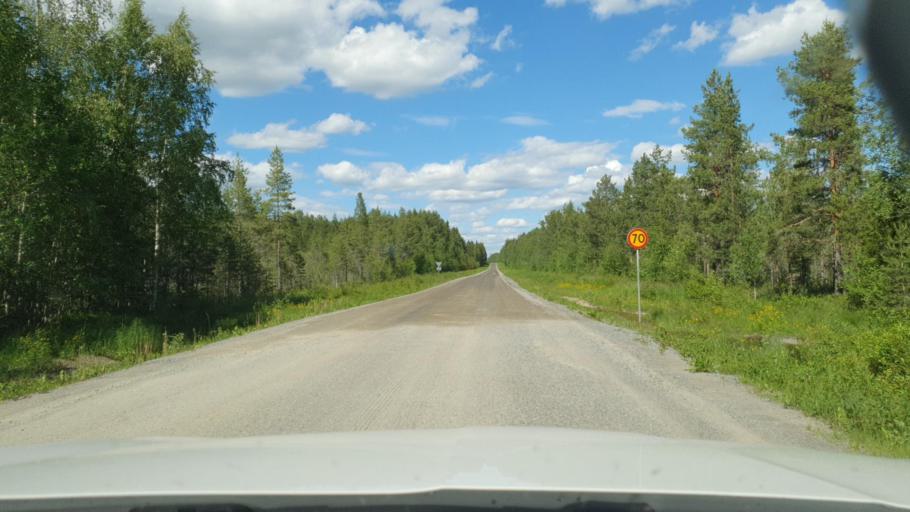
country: SE
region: Vaesterbotten
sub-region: Skelleftea Kommun
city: Forsbacka
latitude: 64.7673
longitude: 20.5180
